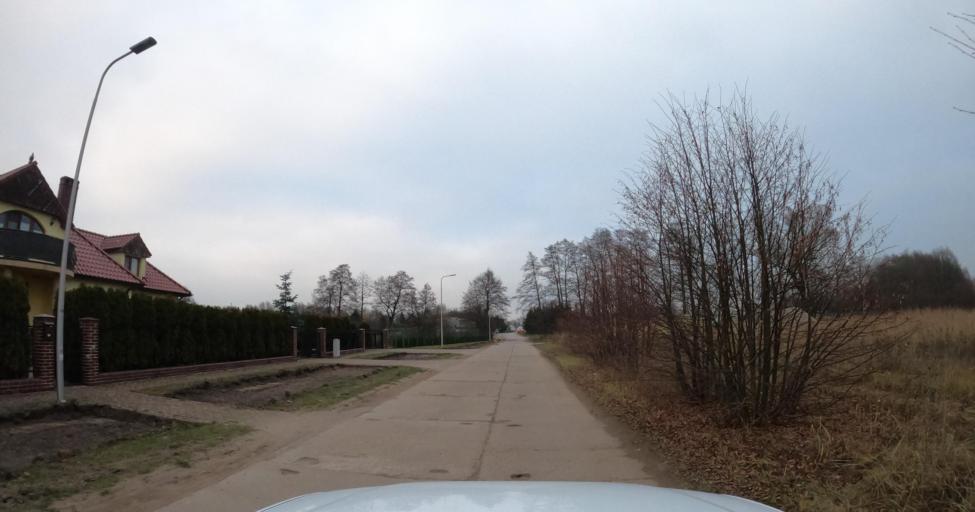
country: PL
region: West Pomeranian Voivodeship
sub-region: Powiat walecki
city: Miroslawiec
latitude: 53.3353
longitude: 16.0884
